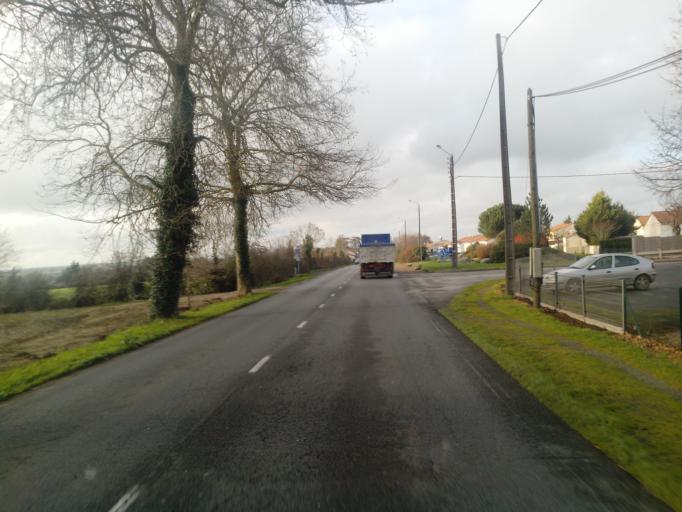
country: FR
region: Poitou-Charentes
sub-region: Departement des Deux-Sevres
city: Chiche
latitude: 46.7939
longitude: -0.3515
